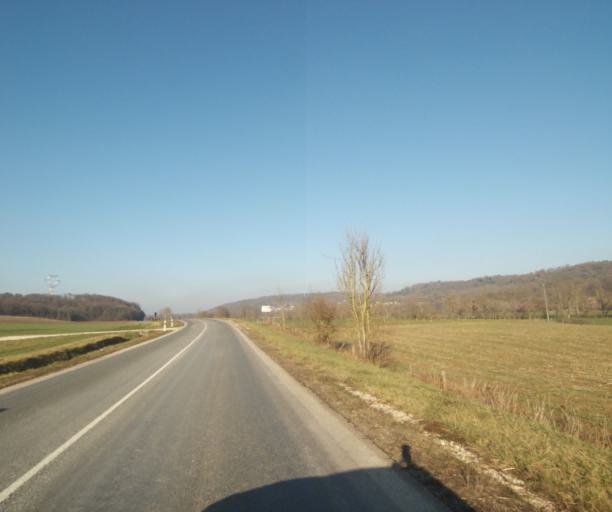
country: FR
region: Champagne-Ardenne
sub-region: Departement de la Haute-Marne
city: Chevillon
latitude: 48.5092
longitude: 5.1129
